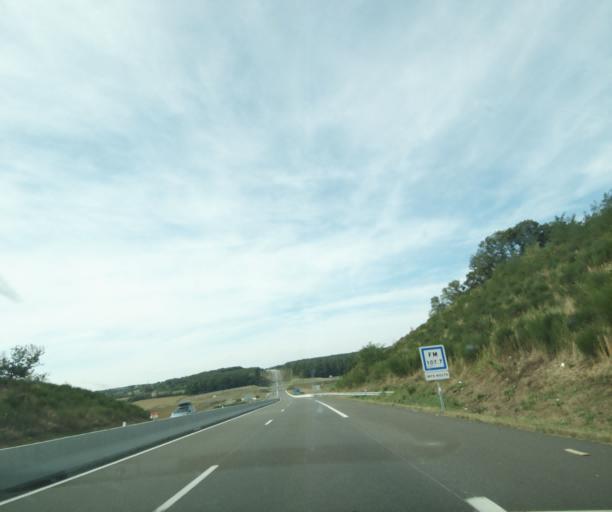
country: FR
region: Auvergne
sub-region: Departement de l'Allier
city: Vendat
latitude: 46.1409
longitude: 3.3416
